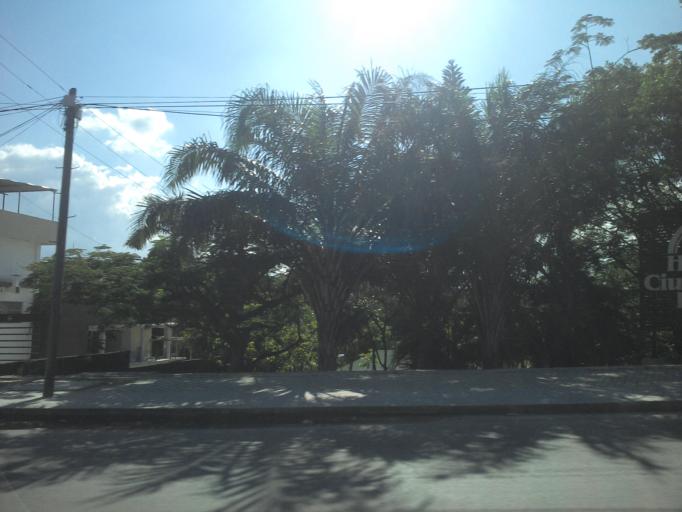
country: MX
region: Chiapas
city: Palenque
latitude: 17.5158
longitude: -91.9933
